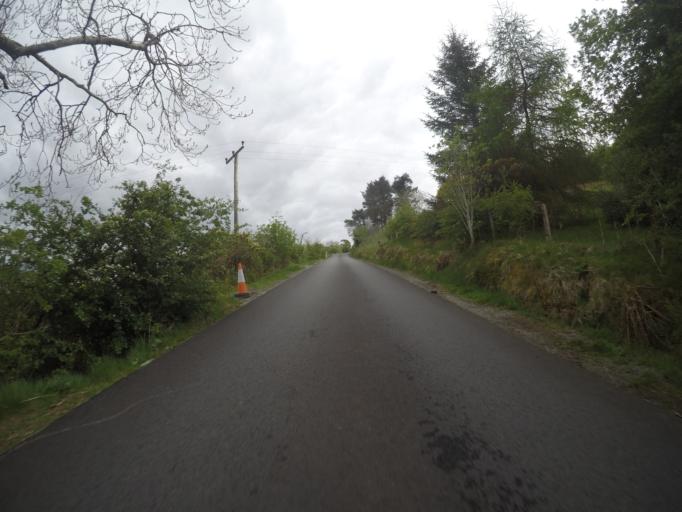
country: GB
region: Scotland
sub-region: Highland
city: Isle of Skye
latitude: 57.3018
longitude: -6.3577
